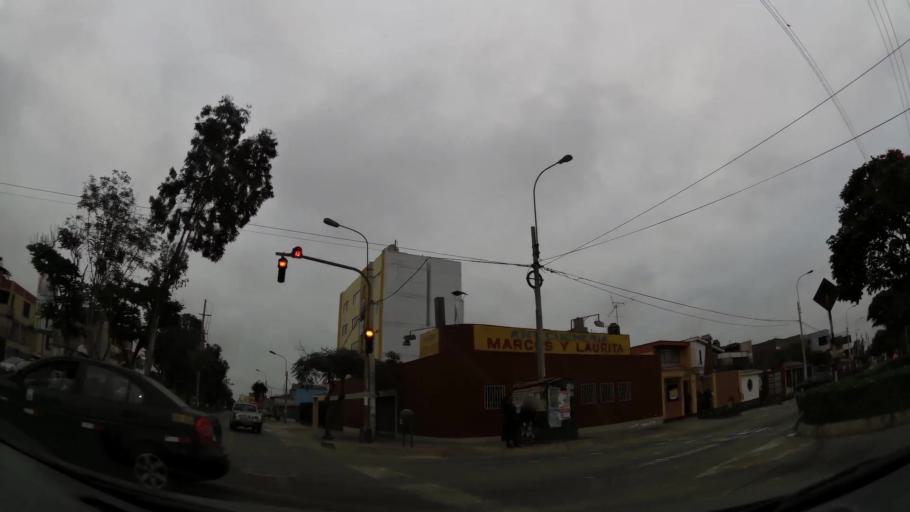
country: PE
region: Lima
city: Lima
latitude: -12.0622
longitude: -77.0665
